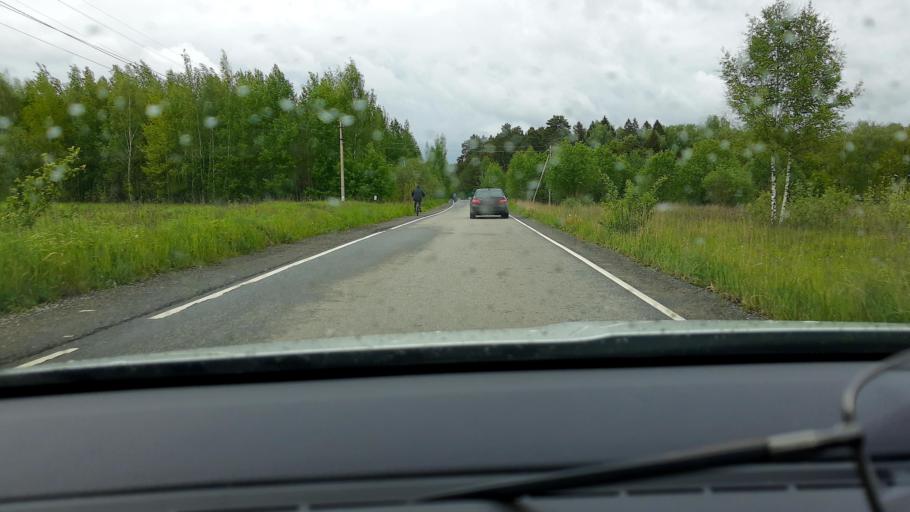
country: RU
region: Moskovskaya
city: Nikolina Gora
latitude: 55.7573
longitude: 36.9812
